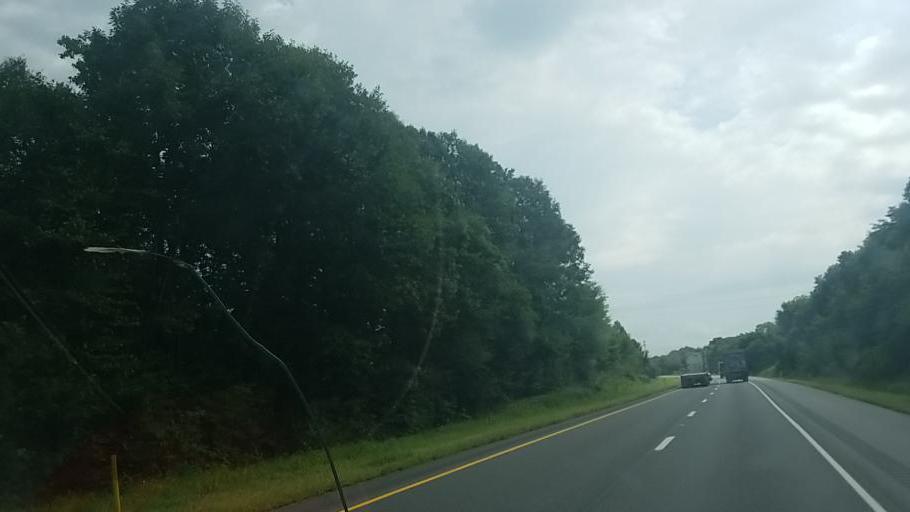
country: US
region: Pennsylvania
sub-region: Juniata County
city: Mifflintown
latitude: 40.5640
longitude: -77.2572
